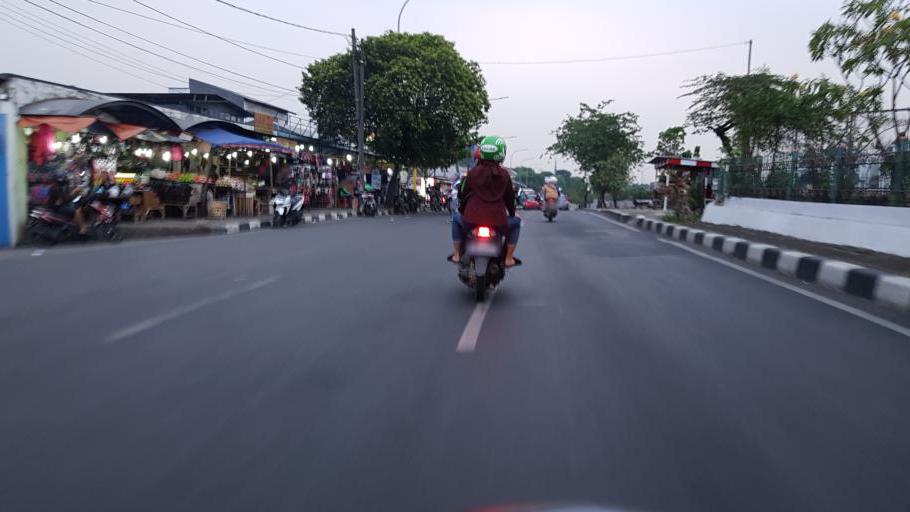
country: ID
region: Jakarta Raya
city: Jakarta
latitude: -6.3083
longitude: 106.8740
